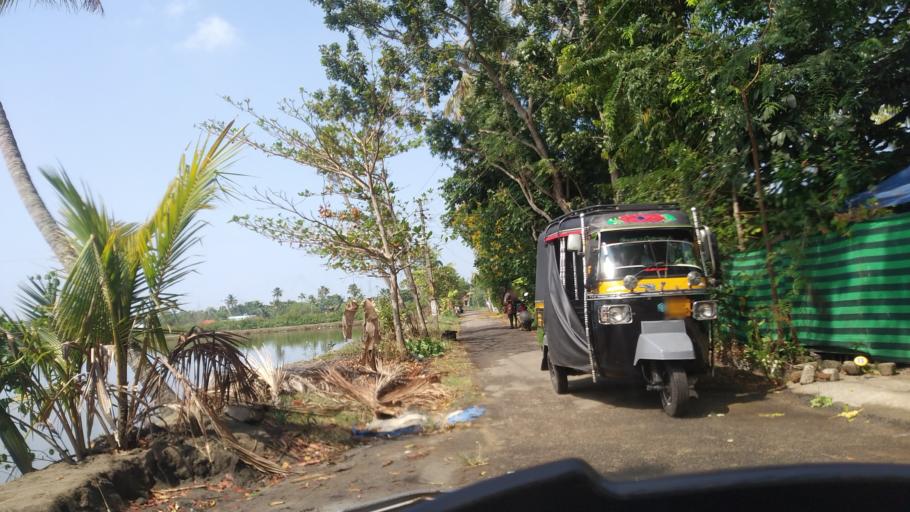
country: IN
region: Kerala
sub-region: Thrissur District
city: Kodungallur
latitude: 10.1350
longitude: 76.2089
